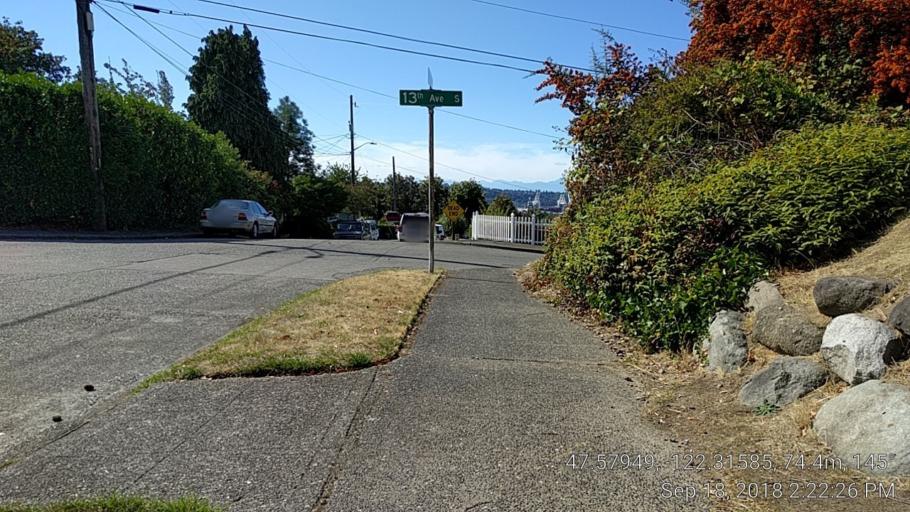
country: US
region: Washington
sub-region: King County
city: Seattle
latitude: 47.5795
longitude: -122.3159
